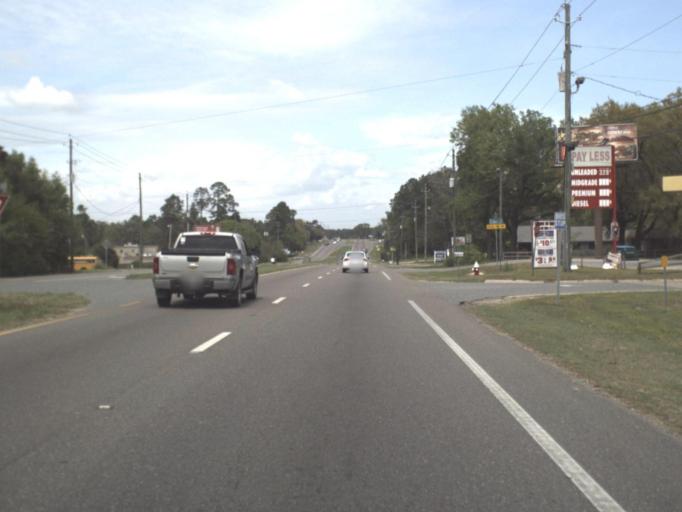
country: US
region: Florida
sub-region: Escambia County
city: Bellview
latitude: 30.4947
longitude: -87.3060
